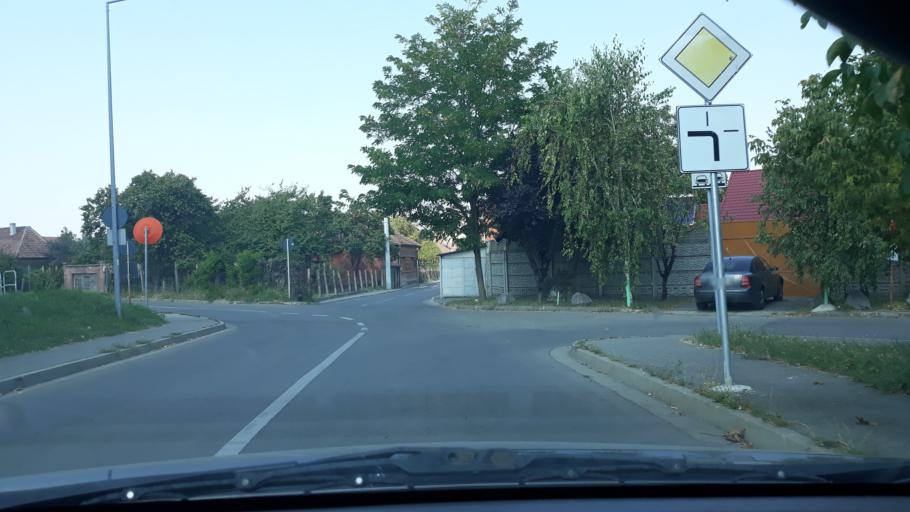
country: RO
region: Bihor
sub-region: Comuna Biharea
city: Oradea
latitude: 47.0402
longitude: 21.9524
